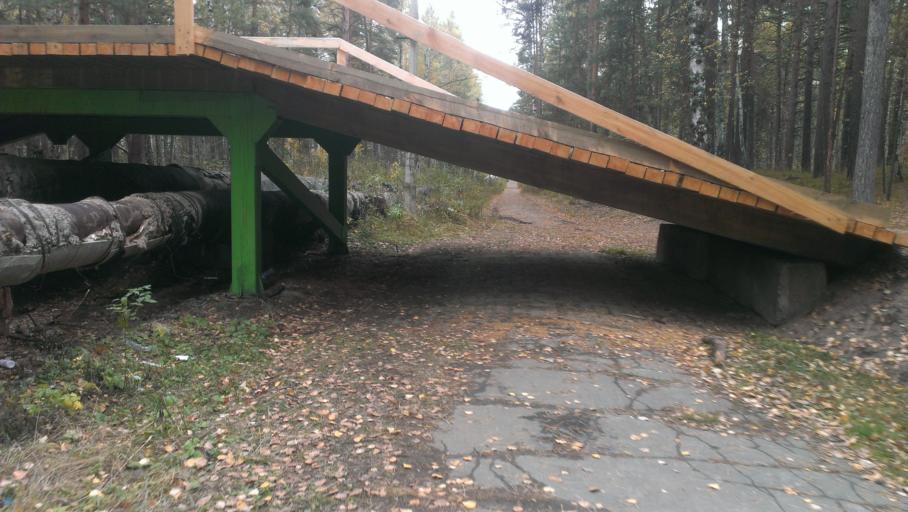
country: RU
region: Altai Krai
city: Yuzhnyy
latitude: 53.2651
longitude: 83.6849
